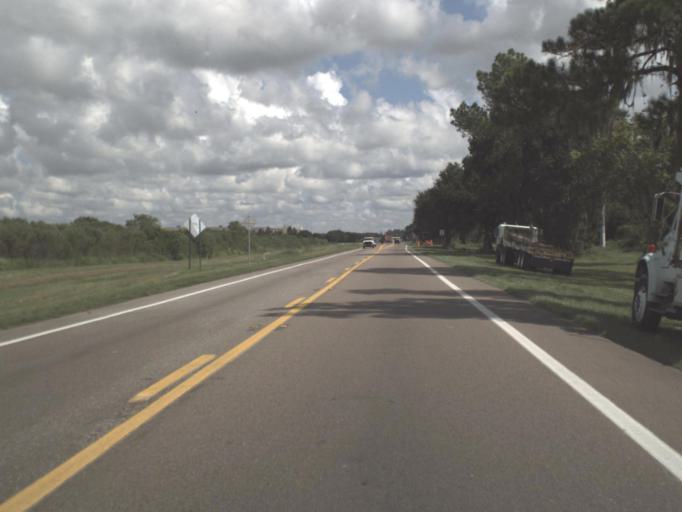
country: US
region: Florida
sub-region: Polk County
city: Combee Settlement
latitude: 28.1247
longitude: -81.9053
